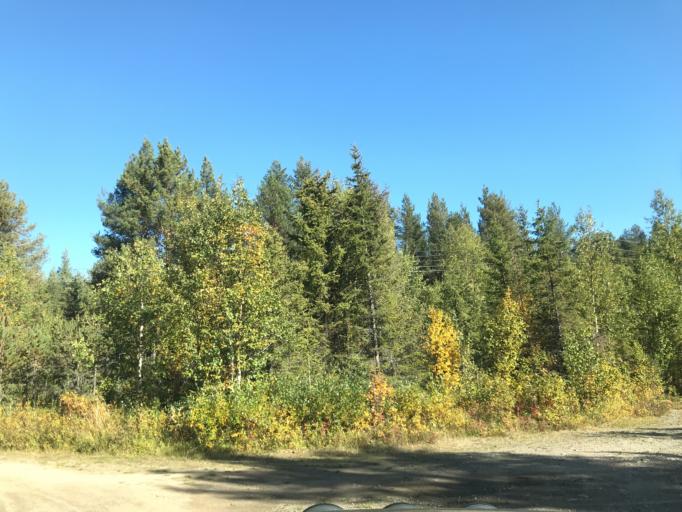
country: SE
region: Norrbotten
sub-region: Gallivare Kommun
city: Malmberget
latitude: 67.6470
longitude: 21.0846
